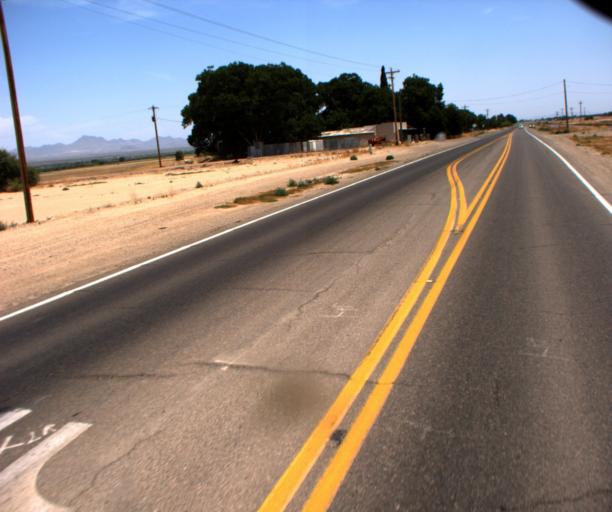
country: US
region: Arizona
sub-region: Graham County
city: Pima
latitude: 32.9189
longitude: -109.8662
